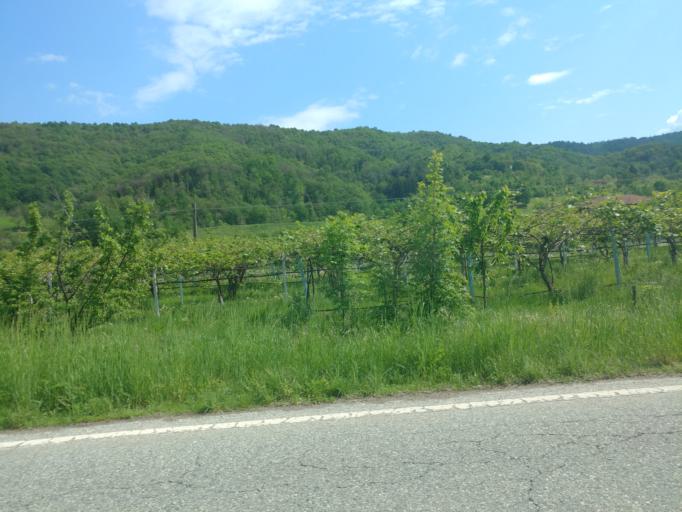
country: IT
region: Piedmont
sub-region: Provincia di Cuneo
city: Castellar
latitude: 44.6226
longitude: 7.4472
